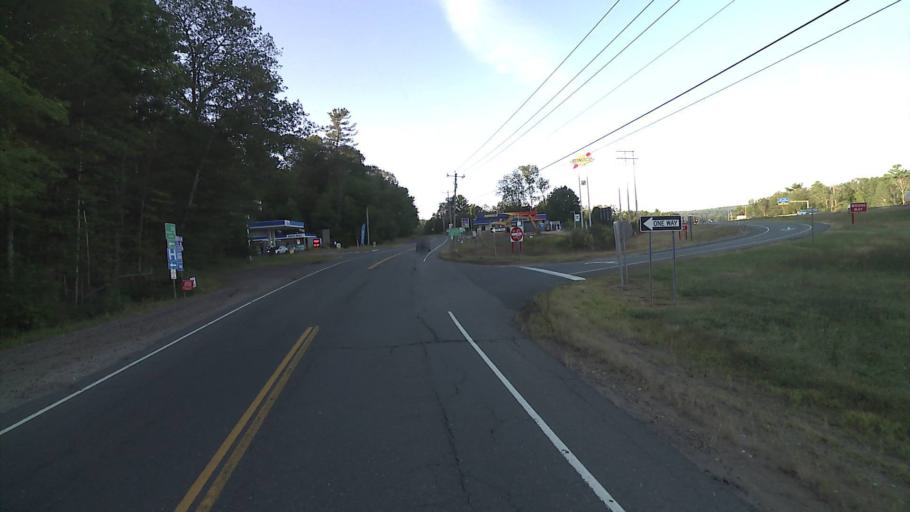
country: US
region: Connecticut
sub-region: Tolland County
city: Stafford Springs
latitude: 41.8980
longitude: -72.2880
